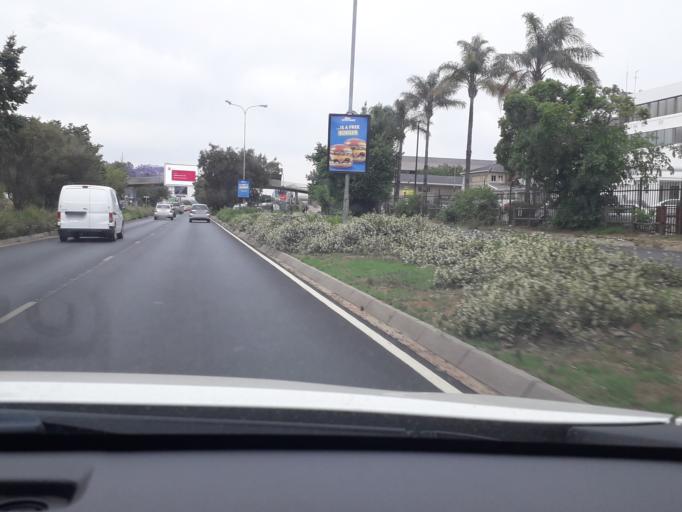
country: ZA
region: Gauteng
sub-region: City of Johannesburg Metropolitan Municipality
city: Midrand
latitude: -26.0528
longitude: 28.0588
